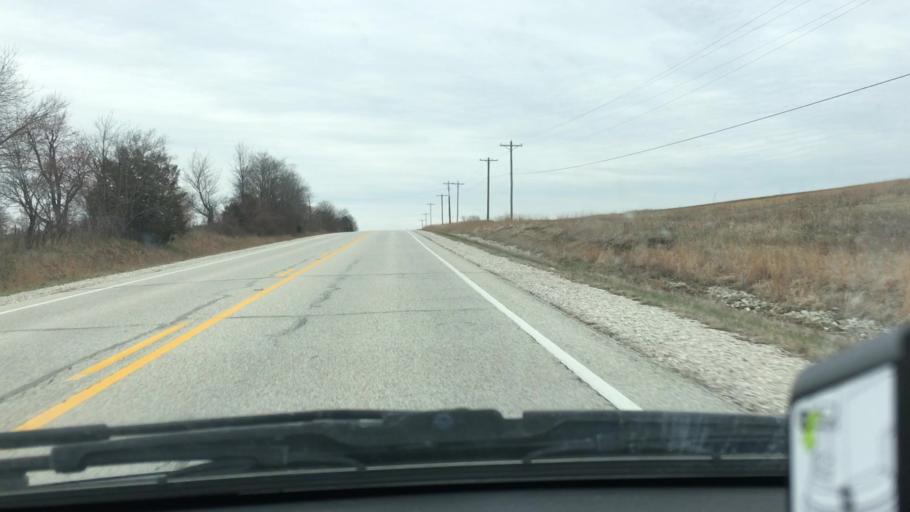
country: US
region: Indiana
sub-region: Greene County
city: Bloomfield
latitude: 39.0126
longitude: -87.0163
